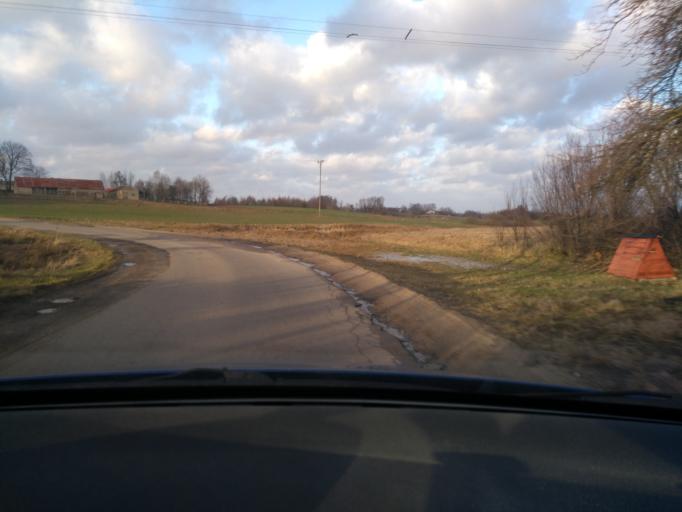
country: PL
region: Pomeranian Voivodeship
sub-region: Powiat kartuski
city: Kartuzy
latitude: 54.3858
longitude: 18.2210
